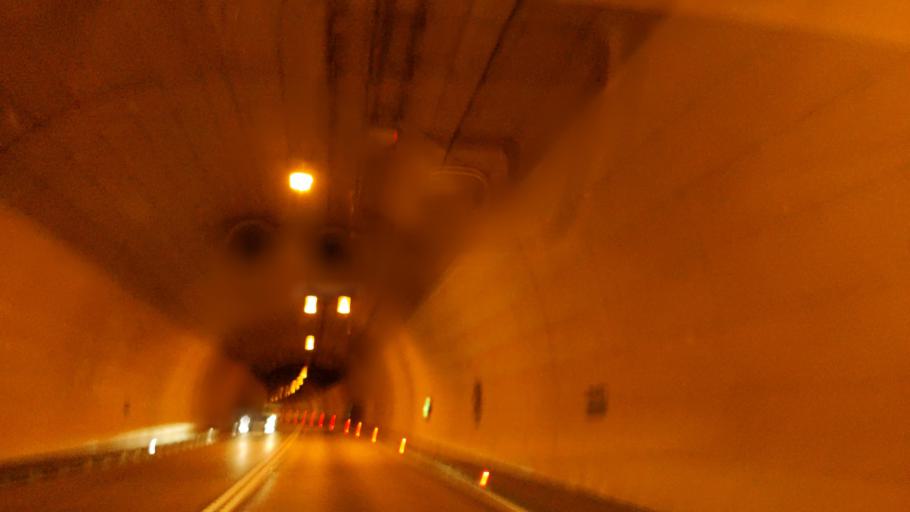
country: AT
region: Vorarlberg
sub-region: Politischer Bezirk Bludenz
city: Dalaas
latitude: 47.1254
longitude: 9.9854
